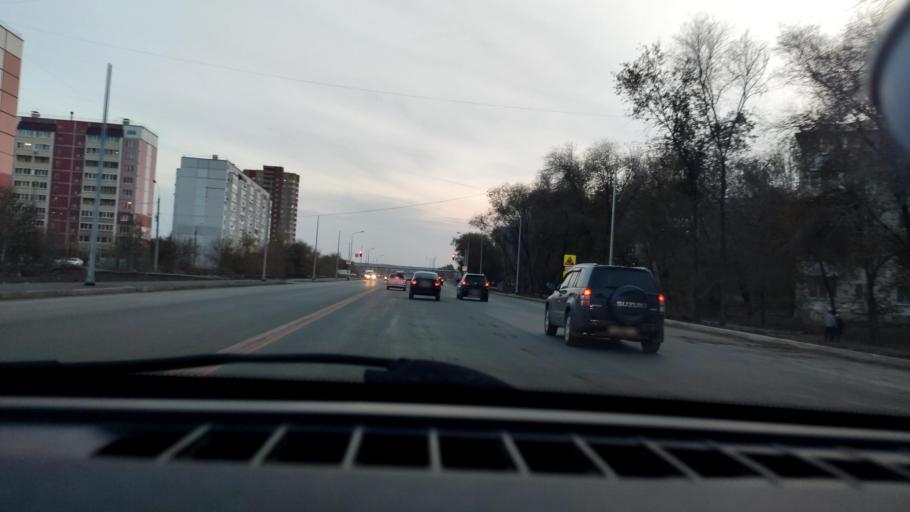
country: RU
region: Samara
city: Samara
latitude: 53.1110
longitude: 50.0822
